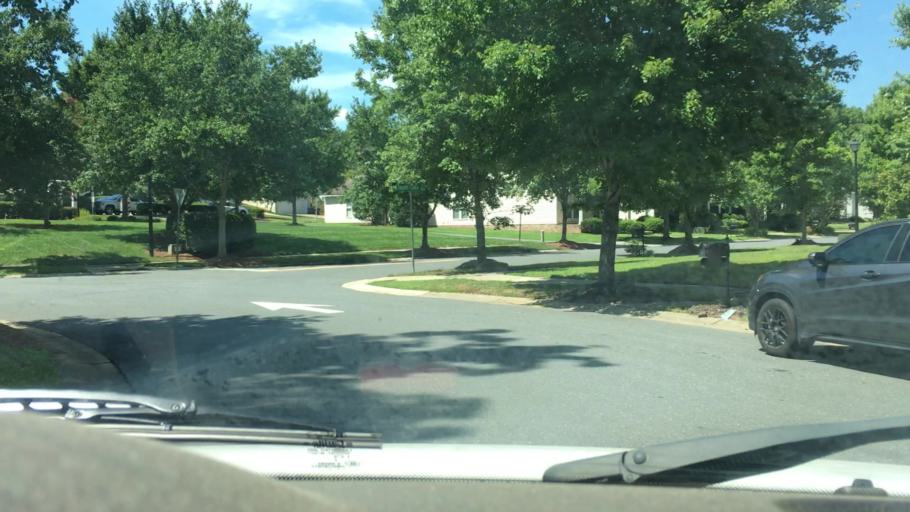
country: US
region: North Carolina
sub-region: Mecklenburg County
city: Huntersville
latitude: 35.3855
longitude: -80.9171
